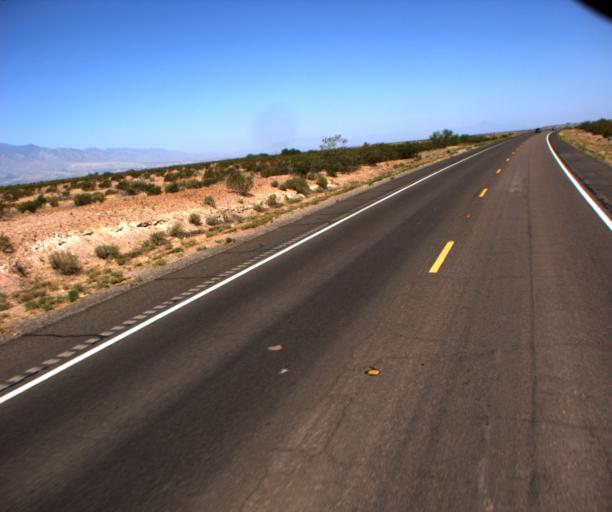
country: US
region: Arizona
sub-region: Graham County
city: Safford
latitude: 32.8035
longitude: -109.5769
